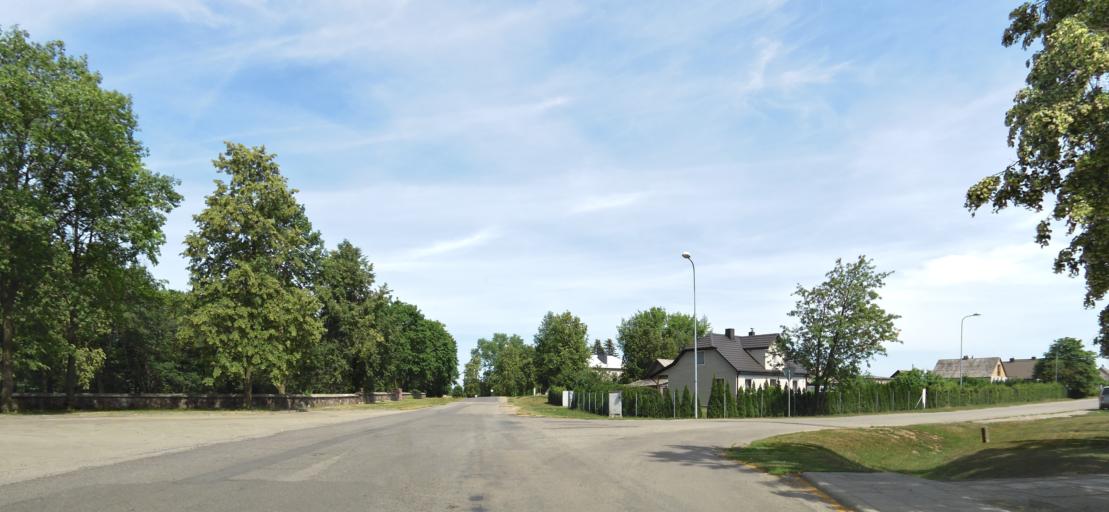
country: LT
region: Panevezys
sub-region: Panevezys City
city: Panevezys
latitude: 55.6526
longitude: 24.2293
